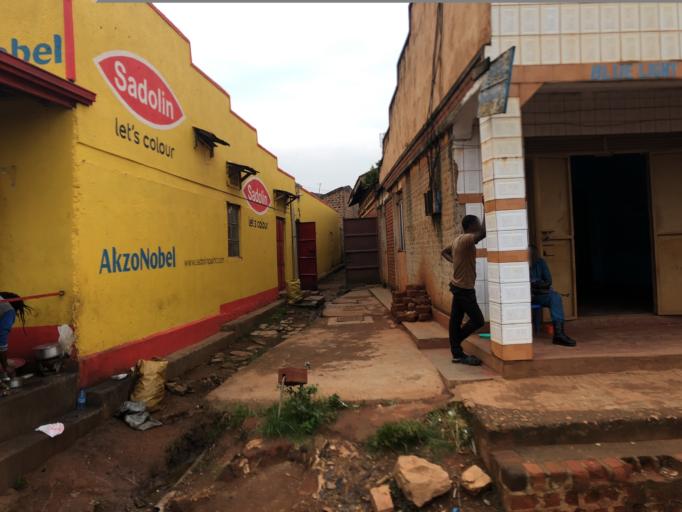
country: UG
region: Central Region
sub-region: Mukono District
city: Mukono
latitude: 0.3532
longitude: 32.7559
